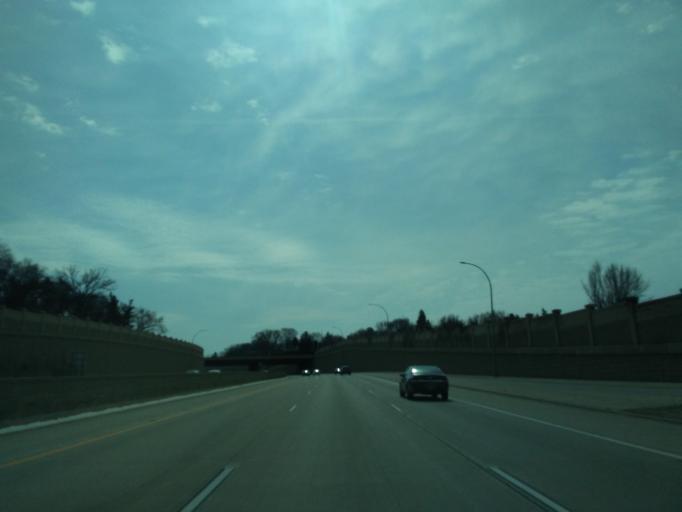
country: US
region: Minnesota
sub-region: Olmsted County
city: Rochester
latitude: 44.0198
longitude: -92.4882
